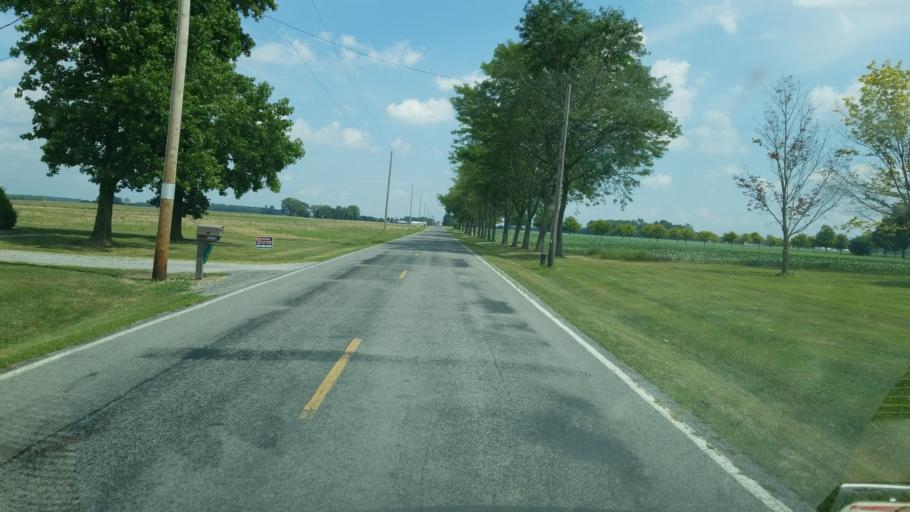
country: US
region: Ohio
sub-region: Hancock County
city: Arlington
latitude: 40.9068
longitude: -83.6705
